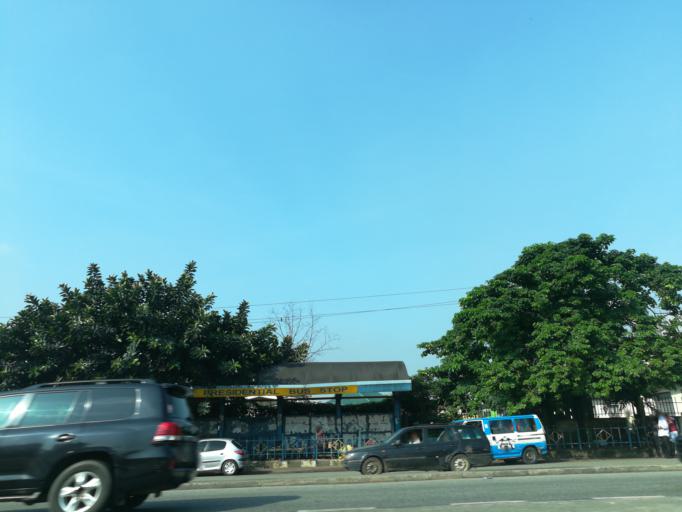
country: NG
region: Rivers
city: Port Harcourt
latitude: 4.8279
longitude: 7.0045
